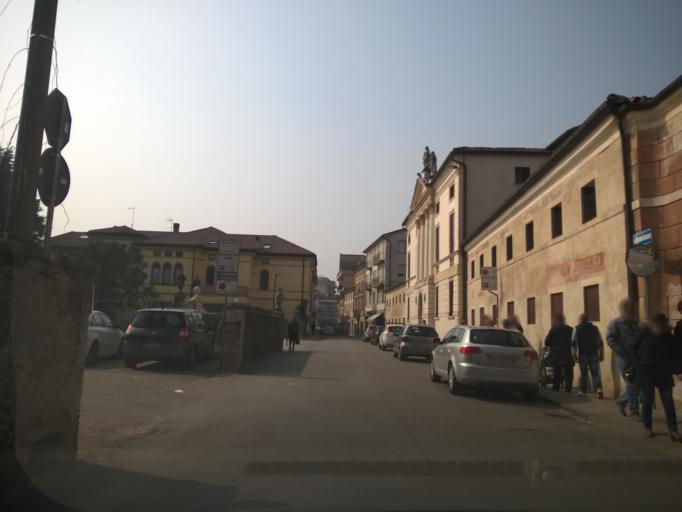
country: IT
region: Veneto
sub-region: Provincia di Vicenza
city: Thiene
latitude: 45.7070
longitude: 11.4820
